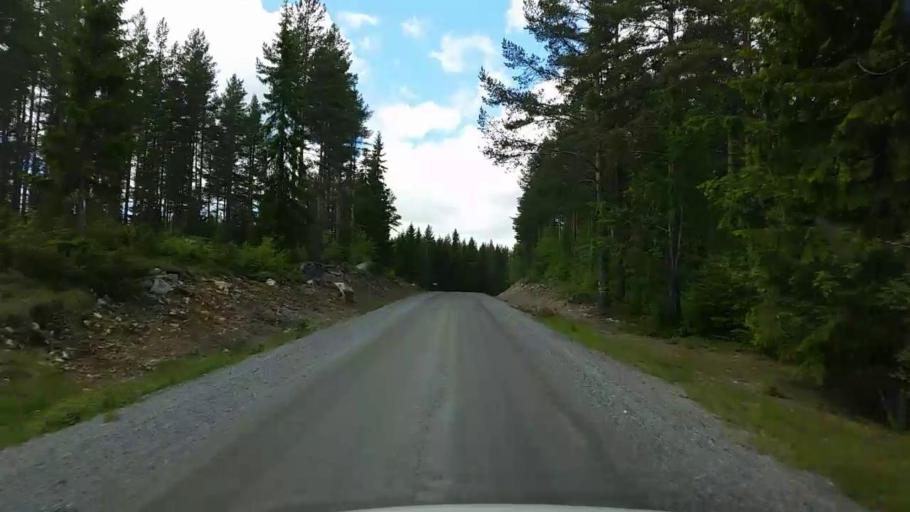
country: SE
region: Gaevleborg
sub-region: Bollnas Kommun
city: Vittsjo
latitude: 61.0684
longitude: 16.2875
